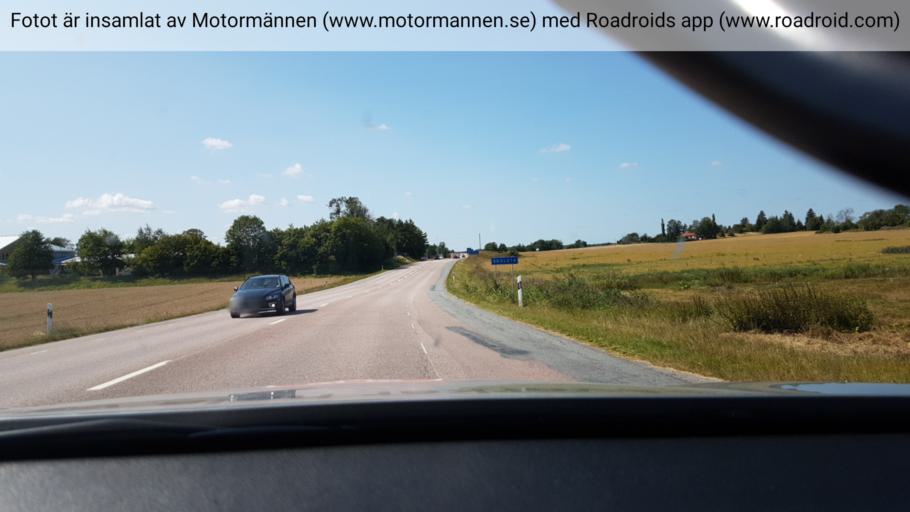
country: SE
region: Uppsala
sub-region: Enkopings Kommun
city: Grillby
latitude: 59.6611
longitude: 17.2504
